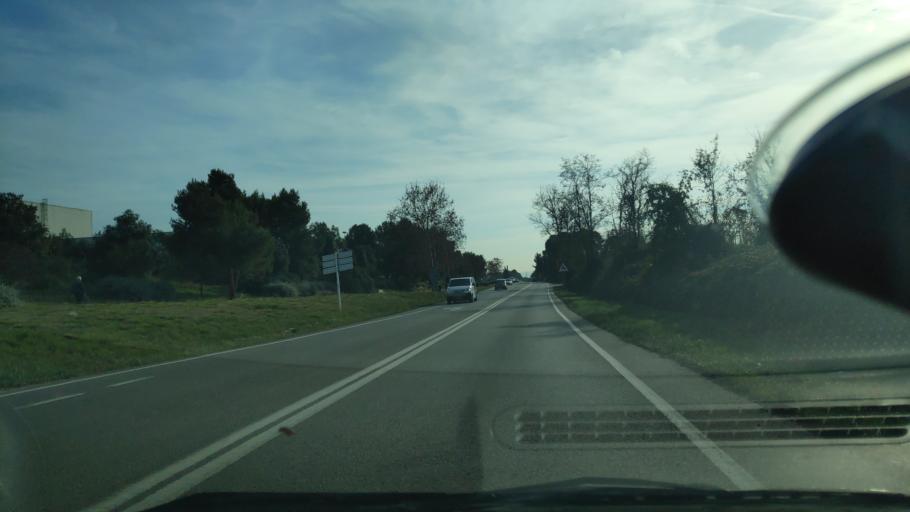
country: ES
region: Catalonia
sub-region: Provincia de Barcelona
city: Castellar del Valles
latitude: 41.5939
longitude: 2.0881
